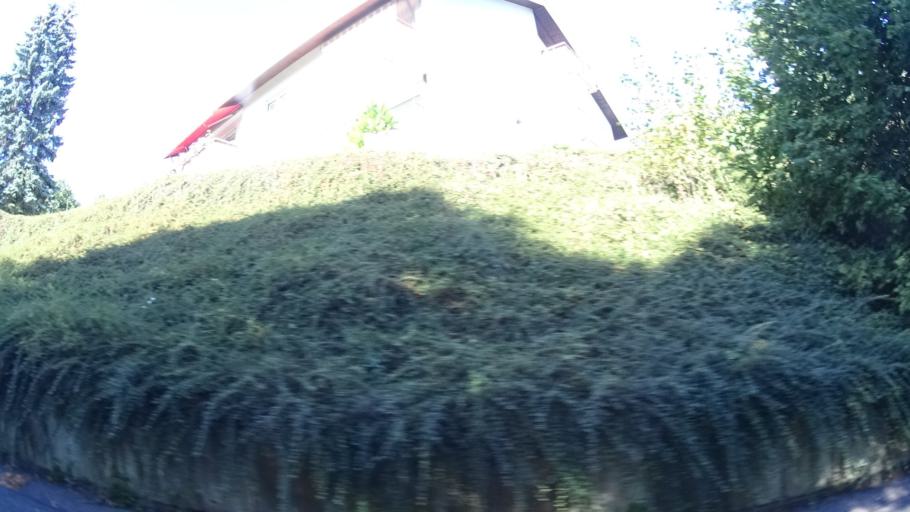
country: DE
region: Baden-Wuerttemberg
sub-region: Karlsruhe Region
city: Ispringen
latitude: 48.8915
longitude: 8.6590
